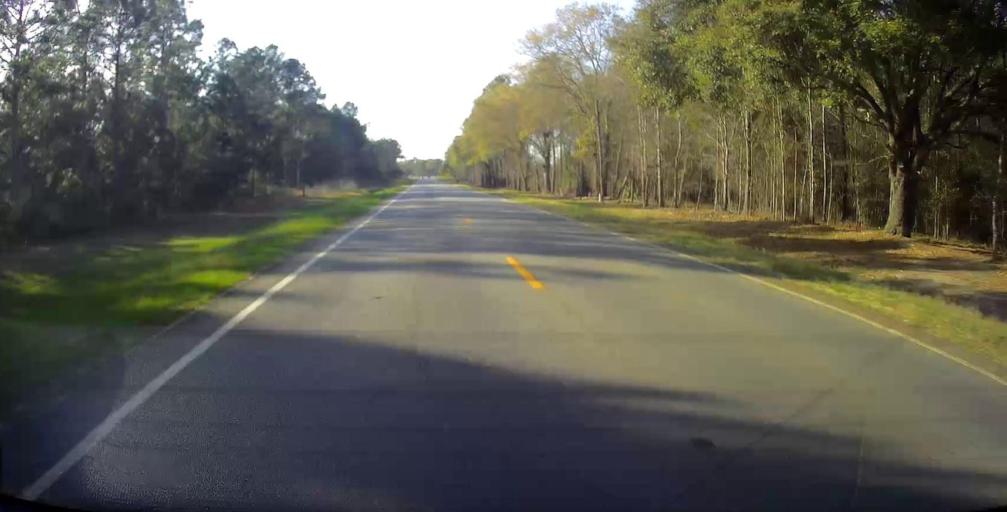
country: US
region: Georgia
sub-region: Toombs County
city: Lyons
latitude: 32.1821
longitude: -82.2939
